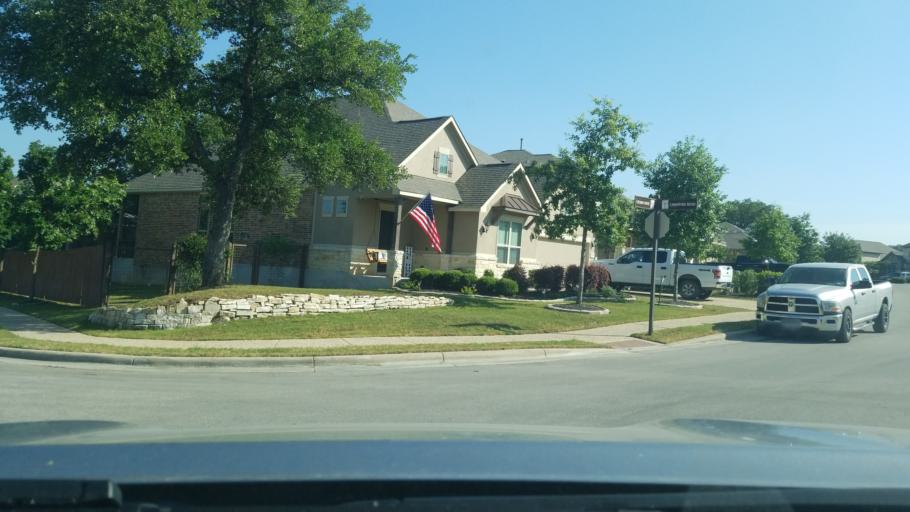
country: US
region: Texas
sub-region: Comal County
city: Bulverde
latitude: 29.7718
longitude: -98.4196
